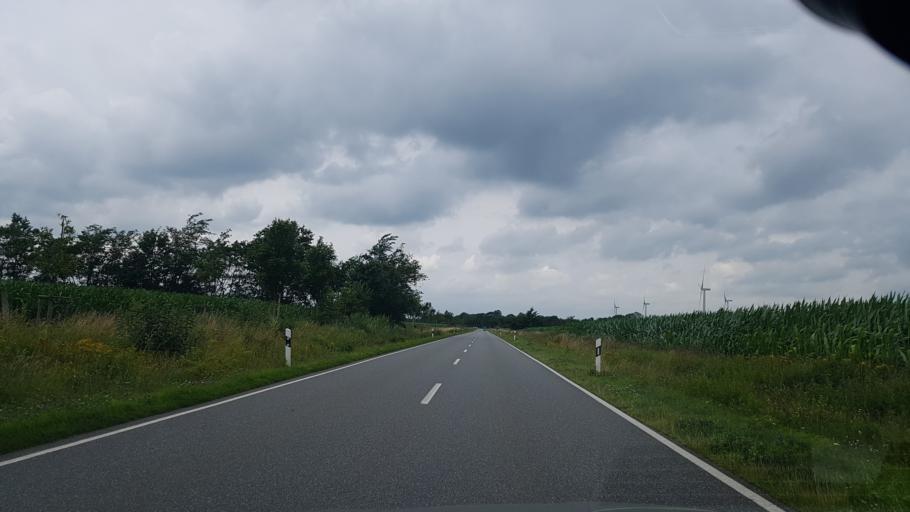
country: DE
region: Schleswig-Holstein
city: Boxlund
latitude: 54.8537
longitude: 9.1828
